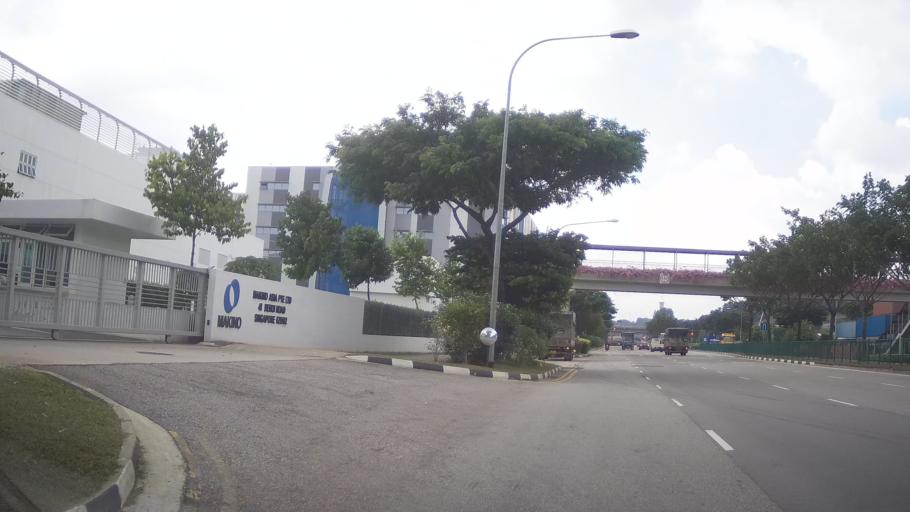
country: MY
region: Johor
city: Johor Bahru
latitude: 1.3180
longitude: 103.6788
